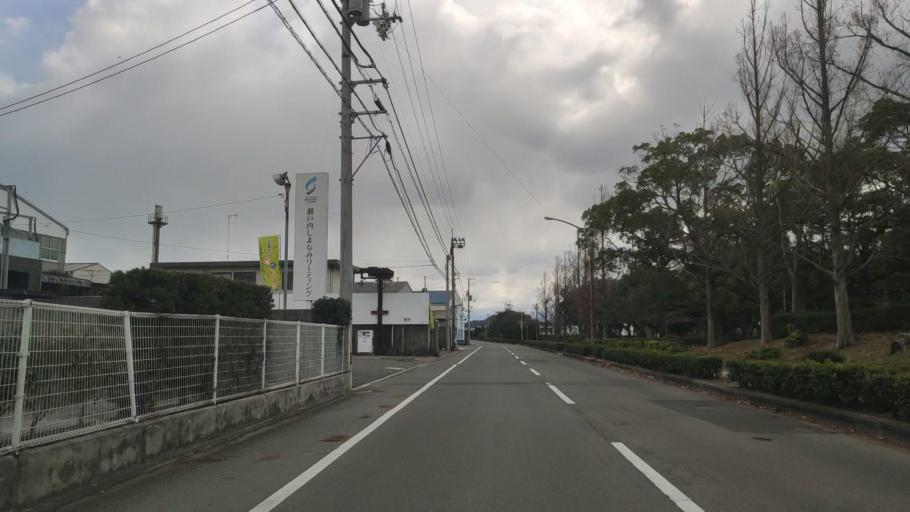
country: JP
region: Ehime
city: Saijo
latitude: 34.0559
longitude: 133.0213
